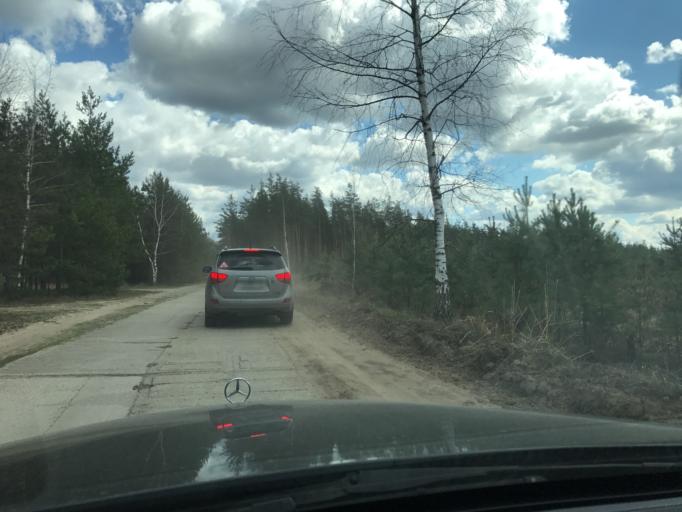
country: RU
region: Vladimir
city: Pokrov
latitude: 55.8464
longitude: 39.1583
